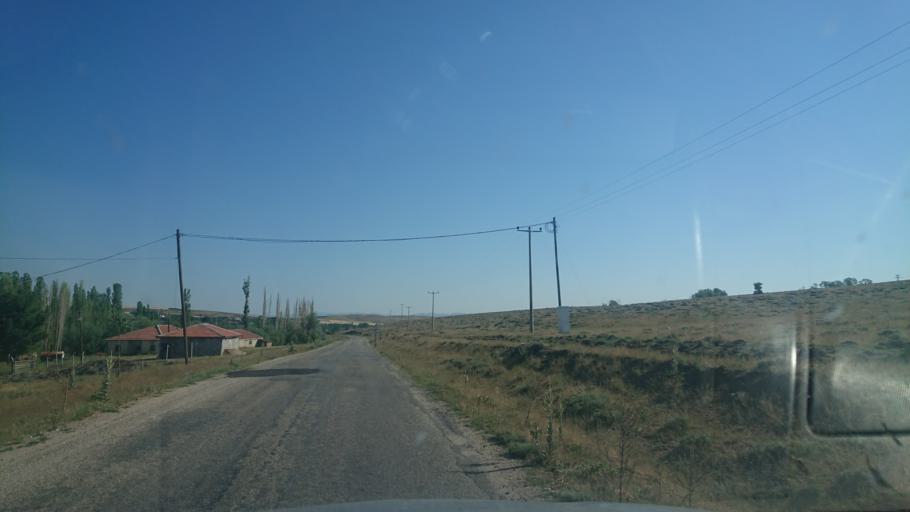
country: TR
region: Aksaray
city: Agacoren
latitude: 38.8738
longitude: 33.8803
